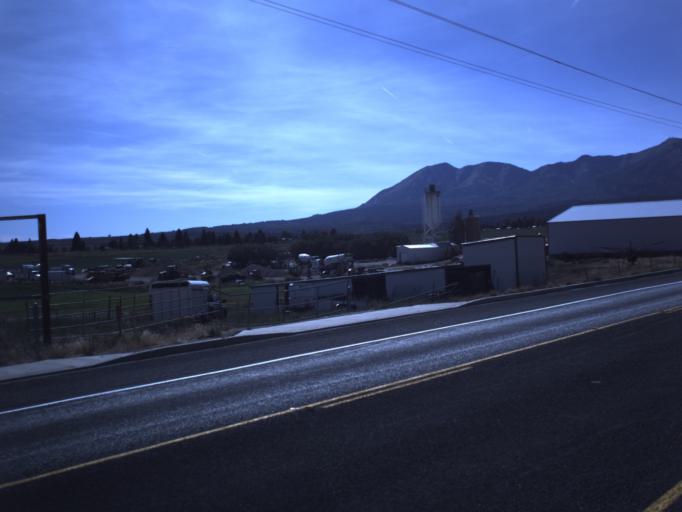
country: US
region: Utah
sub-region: San Juan County
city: Monticello
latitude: 37.8728
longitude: -109.3256
